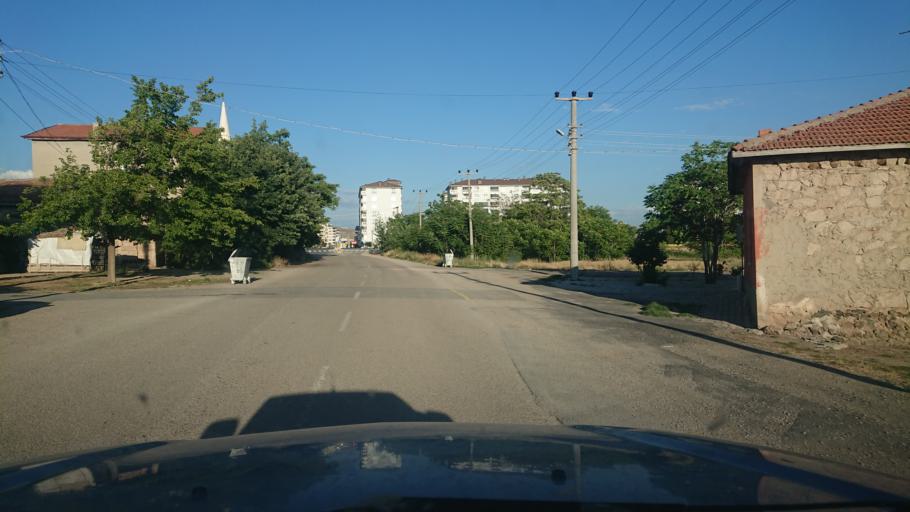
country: TR
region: Aksaray
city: Aksaray
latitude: 38.3891
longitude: 33.9988
